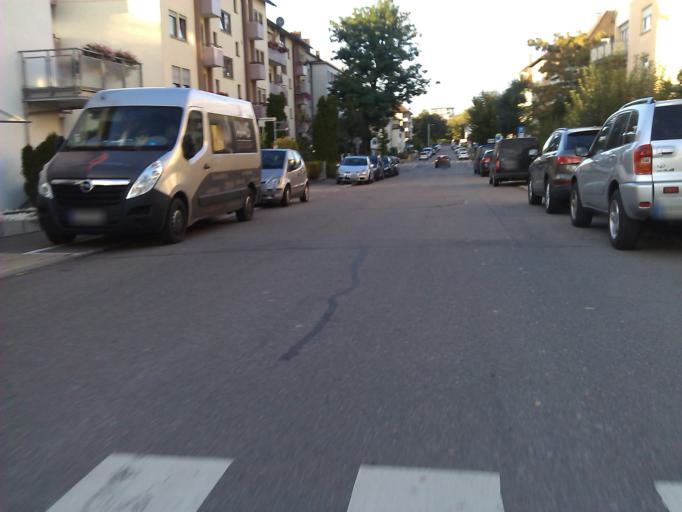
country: DE
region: Baden-Wuerttemberg
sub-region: Regierungsbezirk Stuttgart
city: Heilbronn
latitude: 49.1472
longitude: 9.2255
